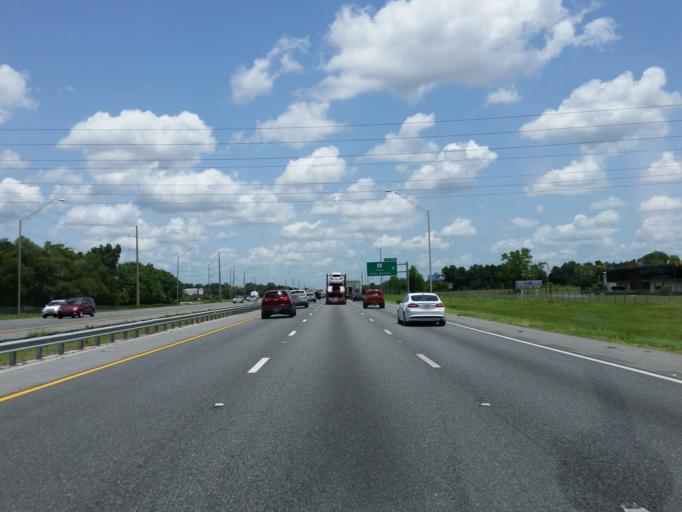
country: US
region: Florida
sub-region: Marion County
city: Ocala
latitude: 29.1795
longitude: -82.1847
